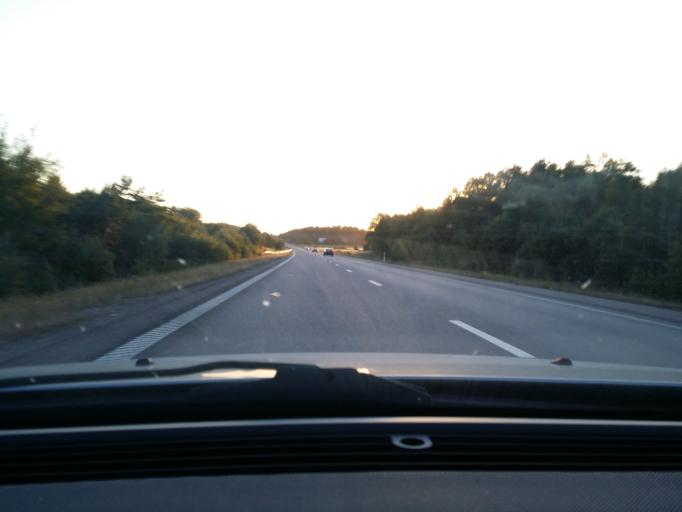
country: SE
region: Uppsala
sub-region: Enkopings Kommun
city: Grillby
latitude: 59.6454
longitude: 17.1862
